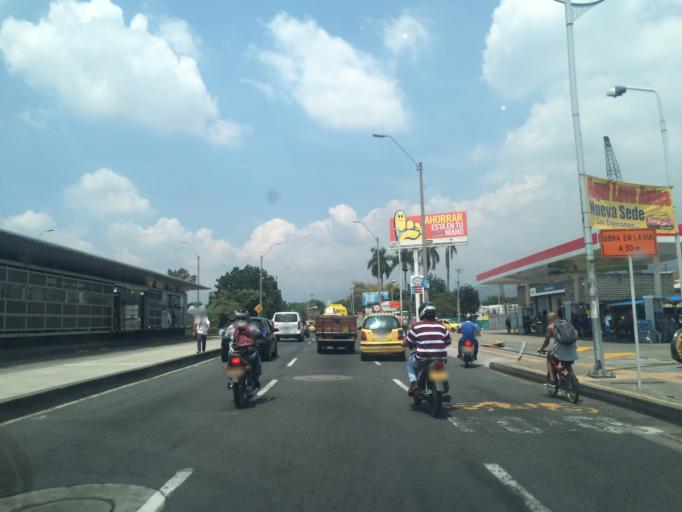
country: CO
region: Valle del Cauca
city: Cali
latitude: 3.4786
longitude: -76.5020
